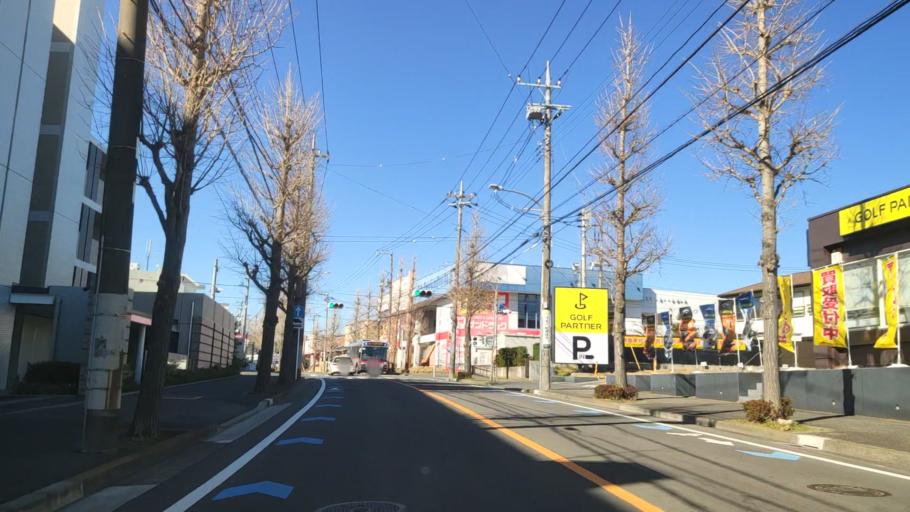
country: JP
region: Tokyo
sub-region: Machida-shi
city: Machida
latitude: 35.5523
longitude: 139.5063
